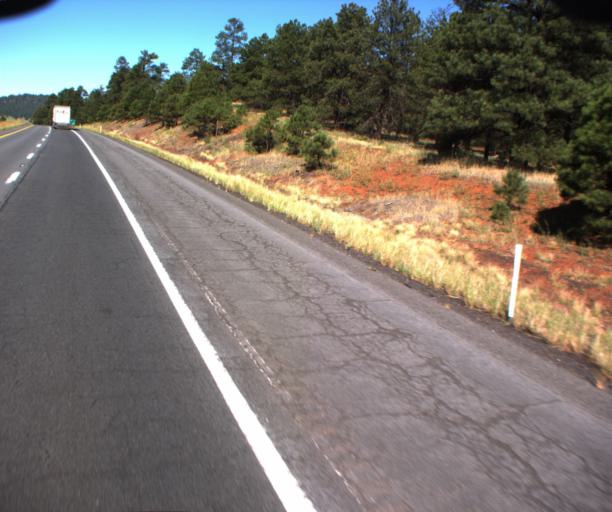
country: US
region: Arizona
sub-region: Coconino County
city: Parks
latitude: 35.2641
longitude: -112.0645
